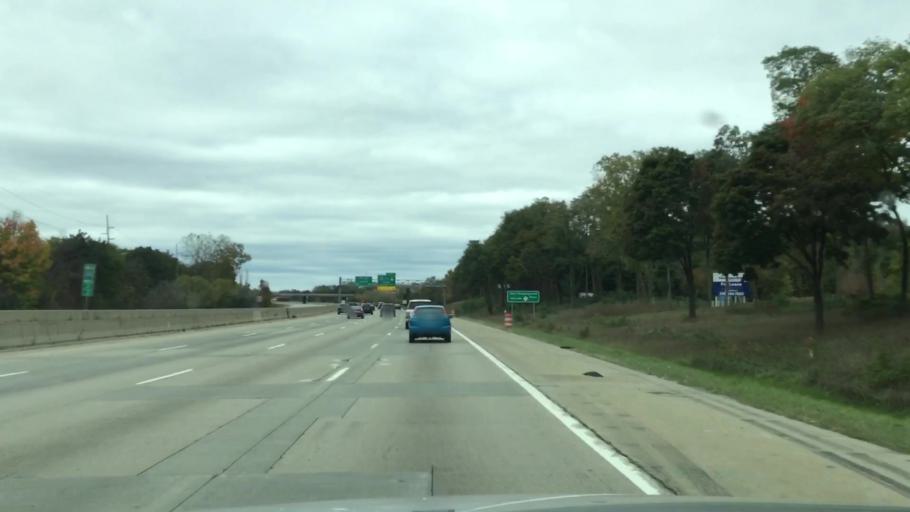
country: US
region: Michigan
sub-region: Oakland County
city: Farmington Hills
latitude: 42.4935
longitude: -83.4081
